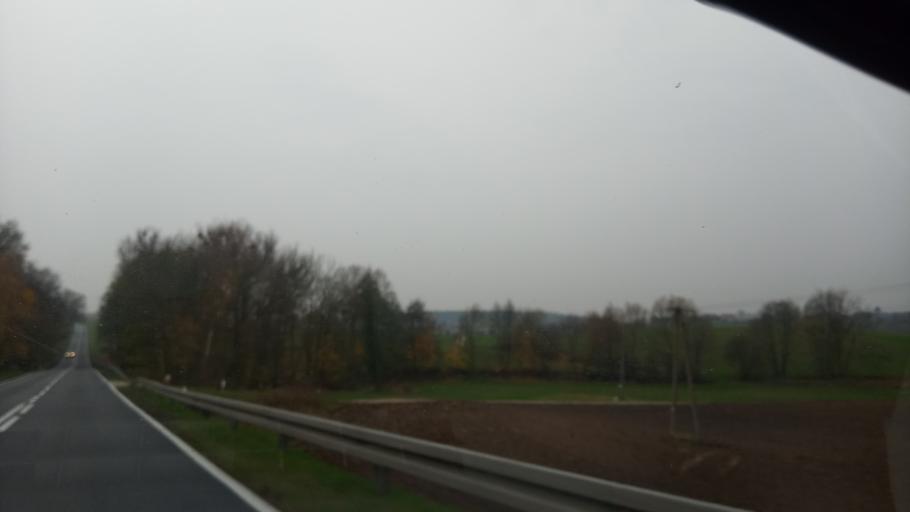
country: PL
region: Kujawsko-Pomorskie
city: Kamien Krajenski
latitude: 53.5583
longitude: 17.5022
